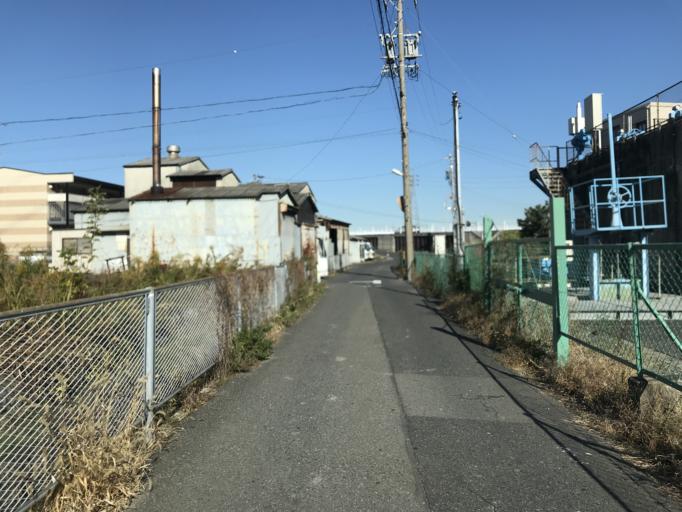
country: JP
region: Aichi
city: Nagoya-shi
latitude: 35.1947
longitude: 136.8387
